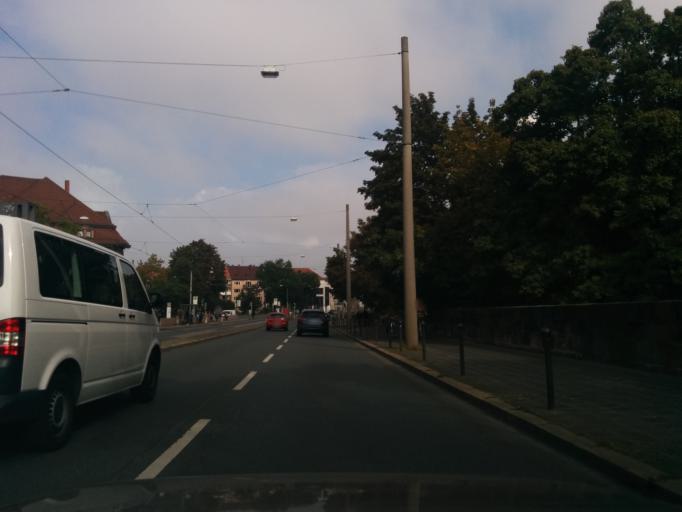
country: DE
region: Bavaria
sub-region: Regierungsbezirk Mittelfranken
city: Nuernberg
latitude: 49.4501
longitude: 11.0661
